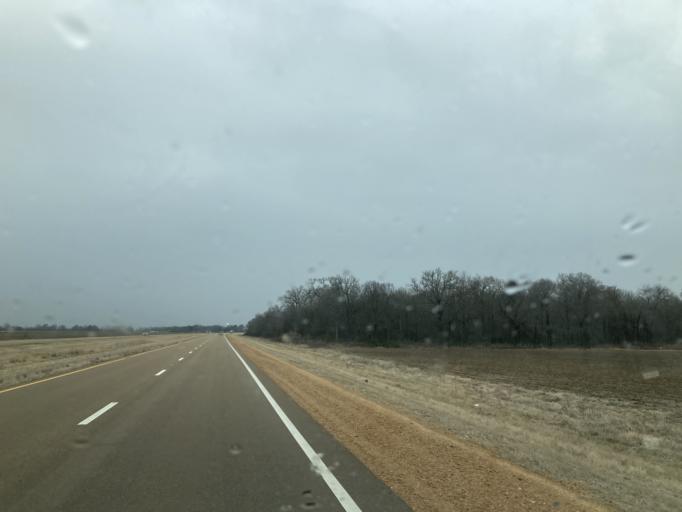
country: US
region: Mississippi
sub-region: Humphreys County
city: Belzoni
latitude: 33.0794
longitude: -90.4807
